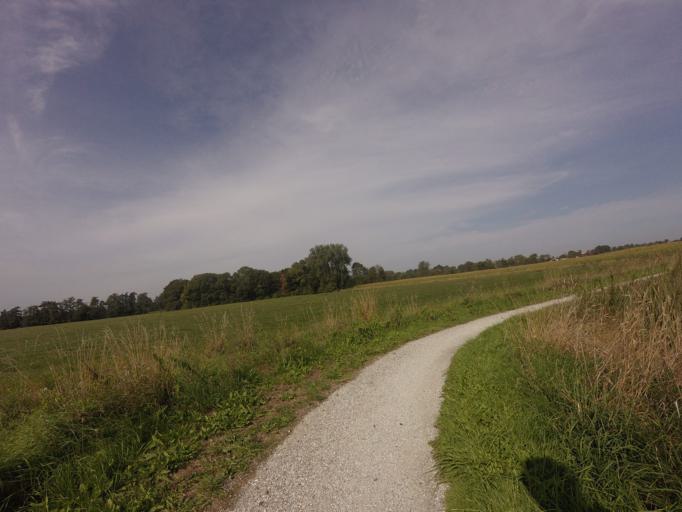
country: NL
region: Groningen
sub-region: Gemeente Zuidhorn
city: Grijpskerk
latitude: 53.2147
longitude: 6.3446
